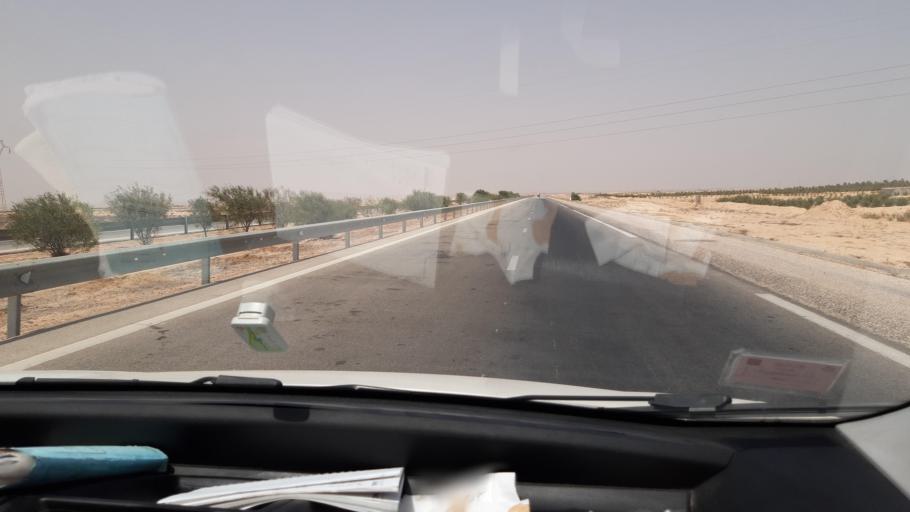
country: TN
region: Qabis
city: Gabes
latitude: 33.9410
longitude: 9.9612
